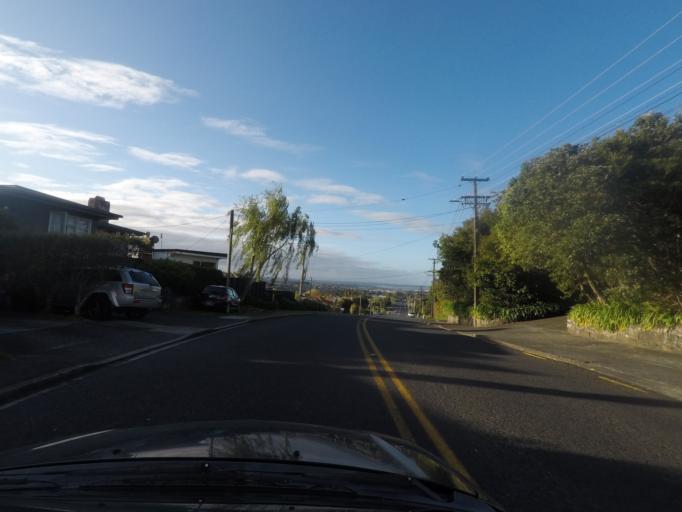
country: NZ
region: Auckland
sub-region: Auckland
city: Waitakere
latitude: -36.9175
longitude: 174.6577
